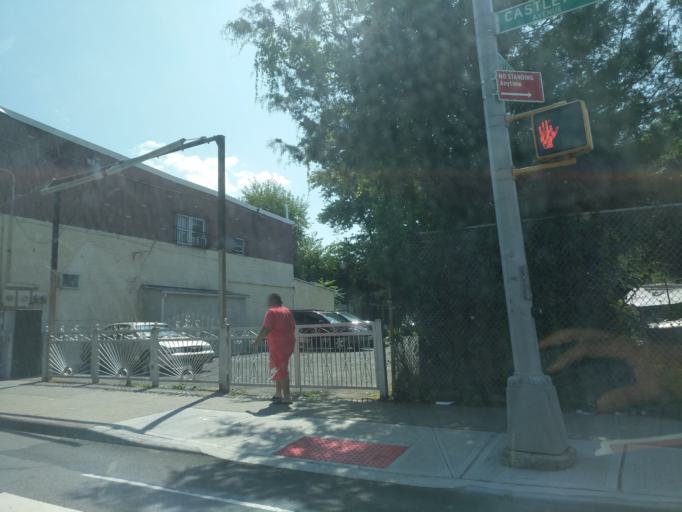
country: US
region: New Jersey
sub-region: Hudson County
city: Bayonne
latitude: 40.6341
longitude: -74.1203
